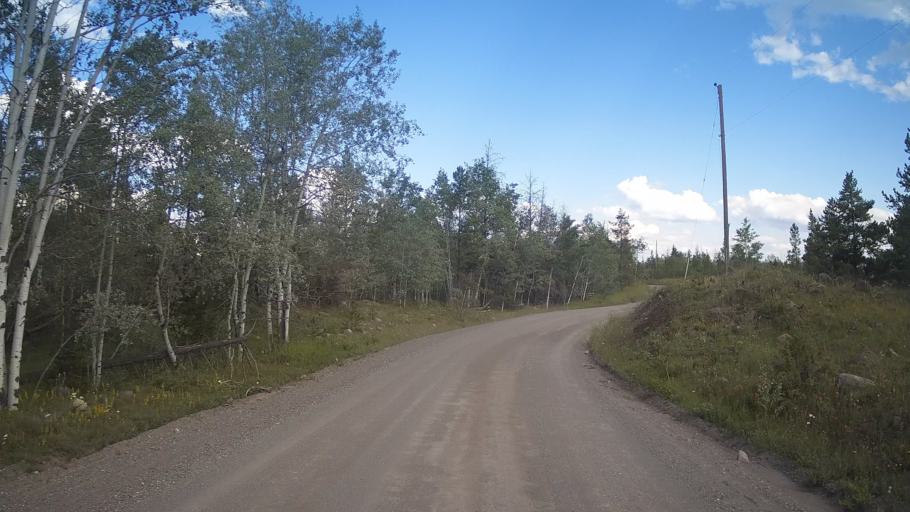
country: CA
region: British Columbia
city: Cache Creek
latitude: 51.2511
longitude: -121.6694
